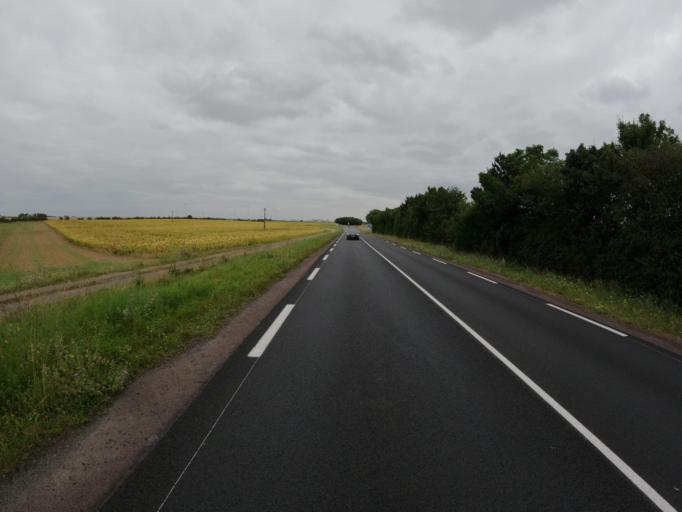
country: FR
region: Pays de la Loire
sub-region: Departement de la Vendee
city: Benet
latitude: 46.3929
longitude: -0.6425
